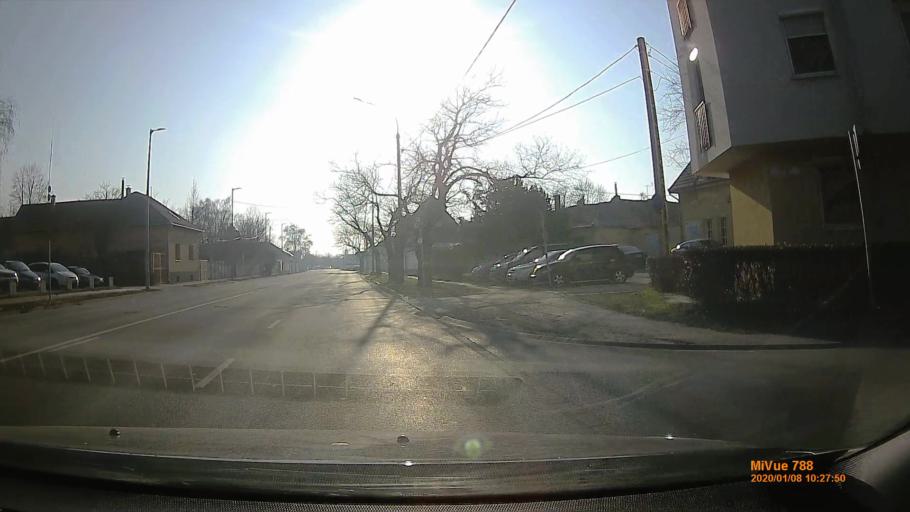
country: HU
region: Bacs-Kiskun
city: Kecskemet
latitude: 46.9061
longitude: 19.7039
